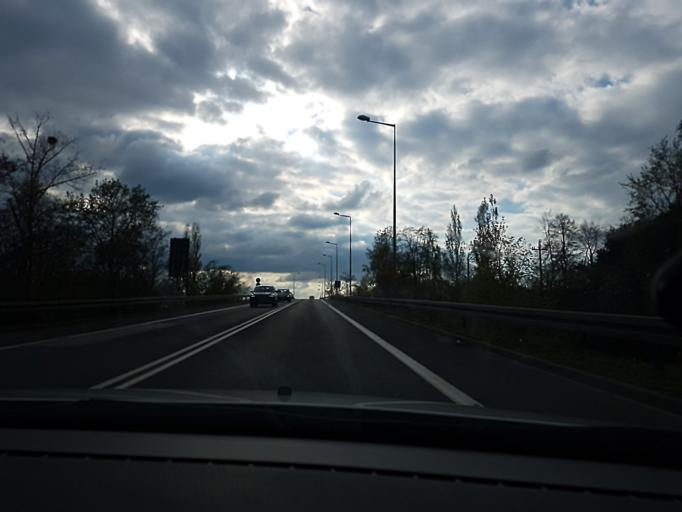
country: PL
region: Lodz Voivodeship
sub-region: powiat Lowicki
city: Lowicz
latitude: 52.1185
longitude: 19.9449
